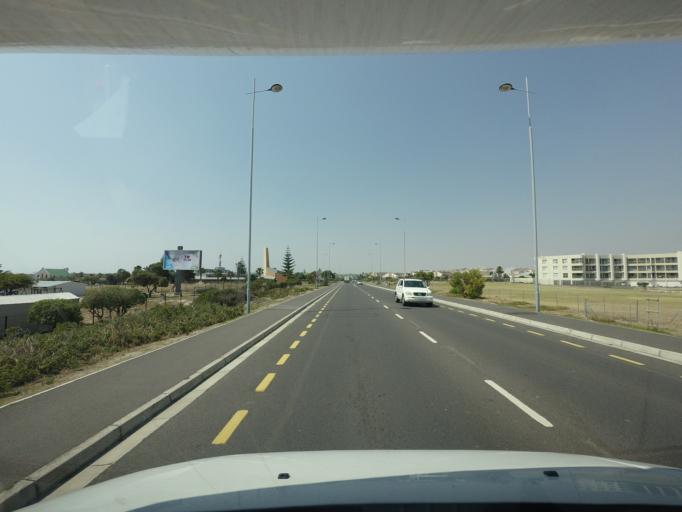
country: ZA
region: Western Cape
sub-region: City of Cape Town
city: Sunset Beach
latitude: -33.7294
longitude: 18.4438
